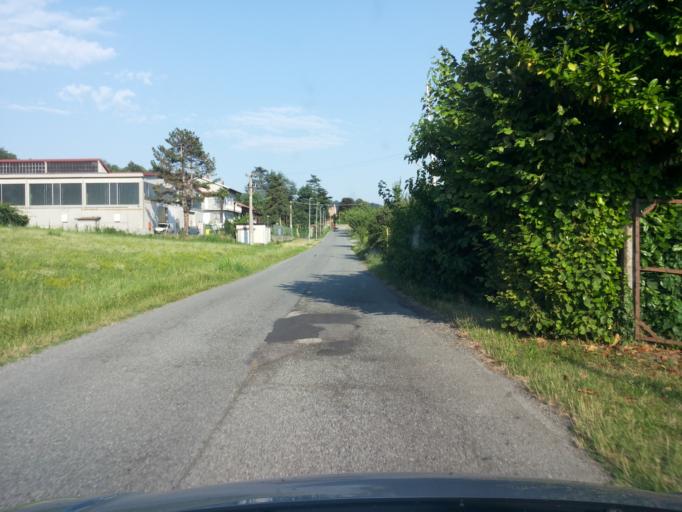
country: IT
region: Piedmont
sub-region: Provincia di Biella
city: Roppolo
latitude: 45.4225
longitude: 8.0611
